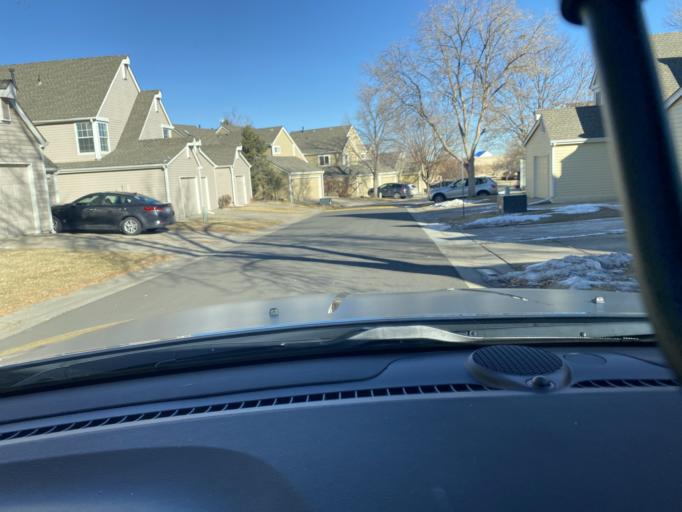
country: US
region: Colorado
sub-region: Jefferson County
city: Applewood
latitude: 39.8113
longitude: -105.1443
